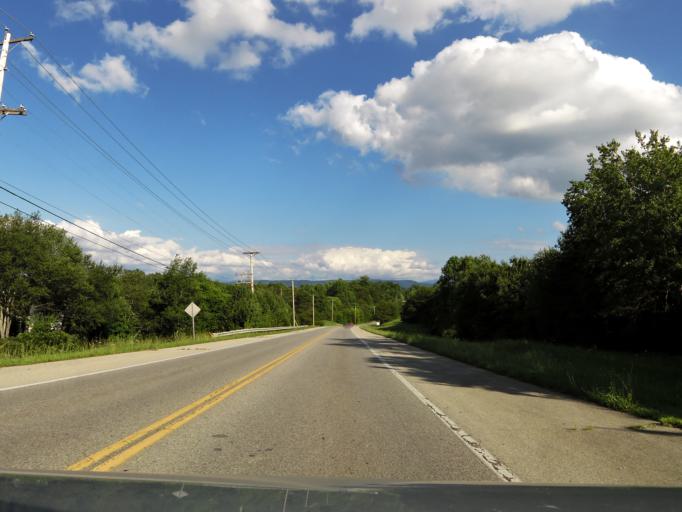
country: US
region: Tennessee
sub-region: Blount County
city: Maryville
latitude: 35.7186
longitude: -84.0250
